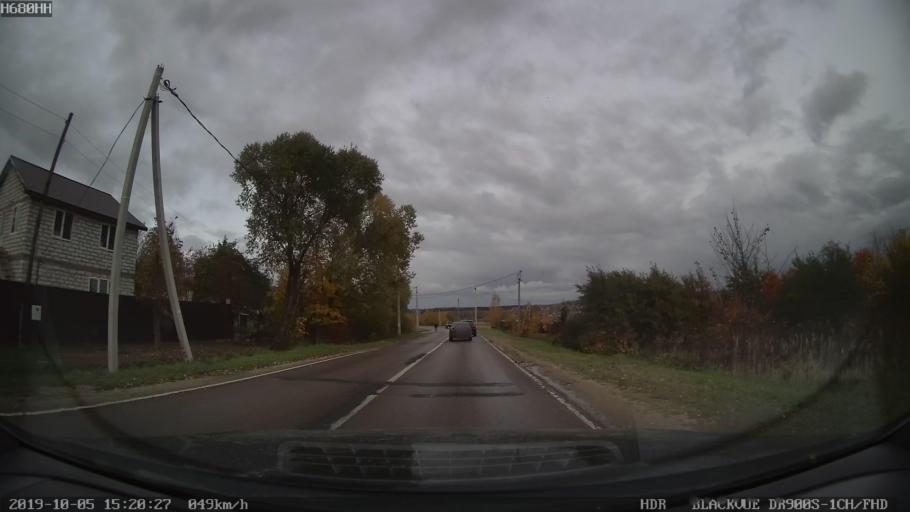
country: RU
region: Moskovskaya
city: Solnechnogorsk
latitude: 56.2233
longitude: 36.9057
